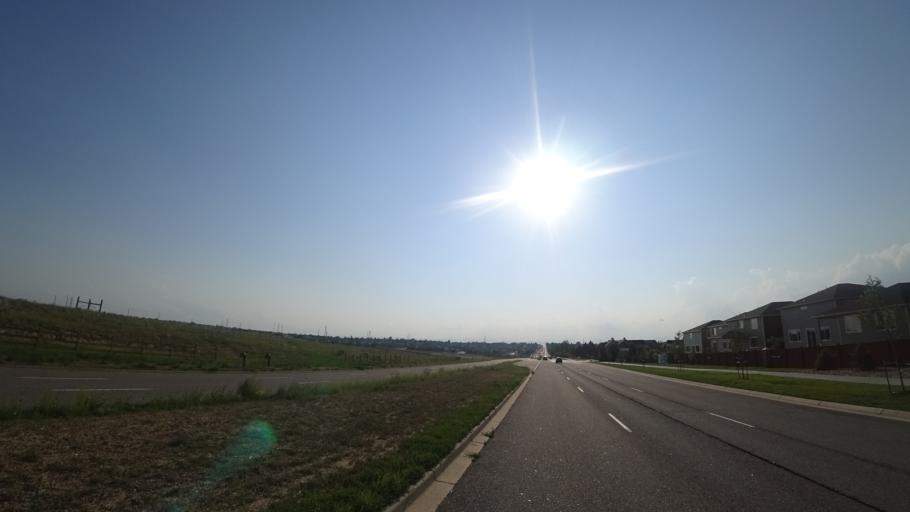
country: US
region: Colorado
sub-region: Arapahoe County
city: Dove Valley
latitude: 39.6385
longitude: -104.7399
